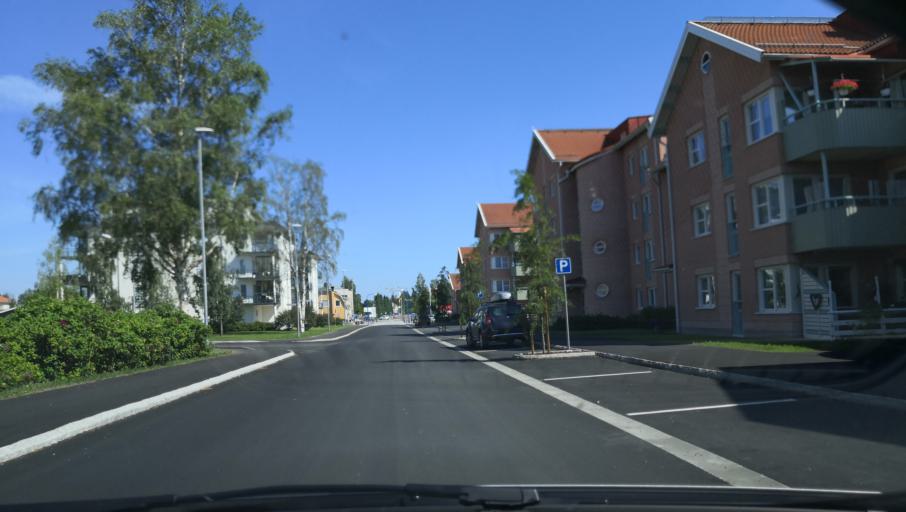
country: SE
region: Gaevleborg
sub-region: Ovanakers Kommun
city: Edsbyn
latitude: 61.3764
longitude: 15.8132
